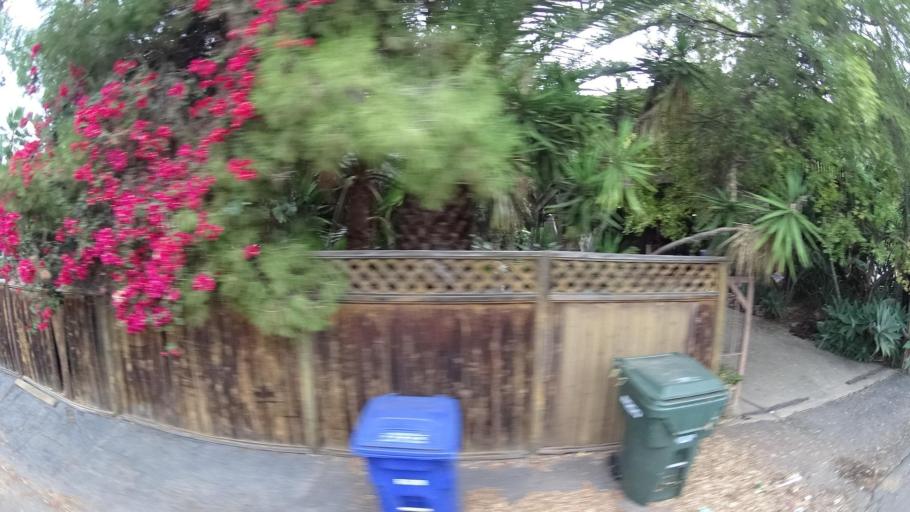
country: US
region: California
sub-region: San Diego County
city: Spring Valley
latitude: 32.7572
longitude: -116.9958
